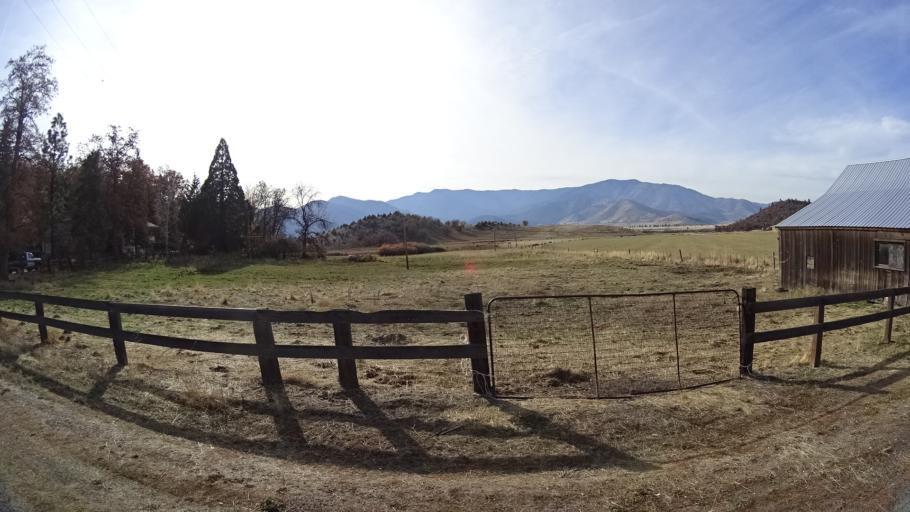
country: US
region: California
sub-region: Siskiyou County
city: Weed
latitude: 41.4670
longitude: -122.4138
